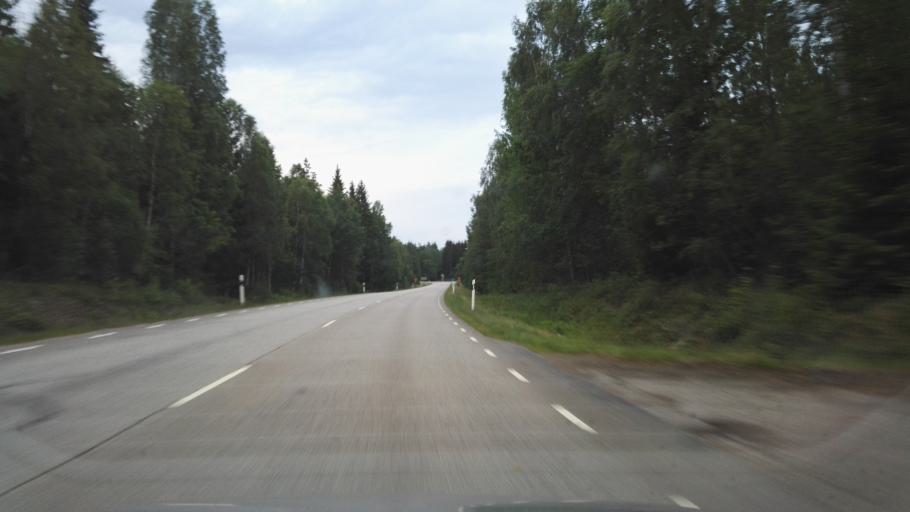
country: SE
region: Kronoberg
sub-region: Vaxjo Kommun
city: Braas
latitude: 57.0378
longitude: 15.0685
